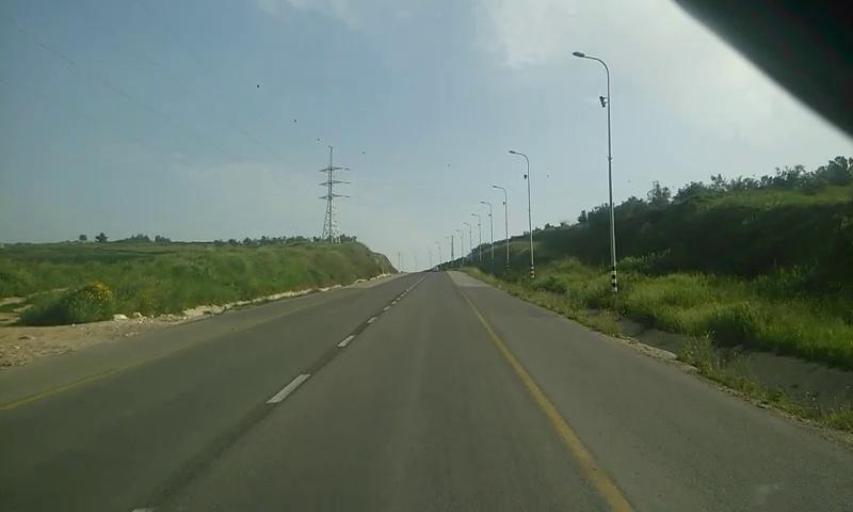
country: PS
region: West Bank
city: Sarrah
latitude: 32.1993
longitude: 35.1851
